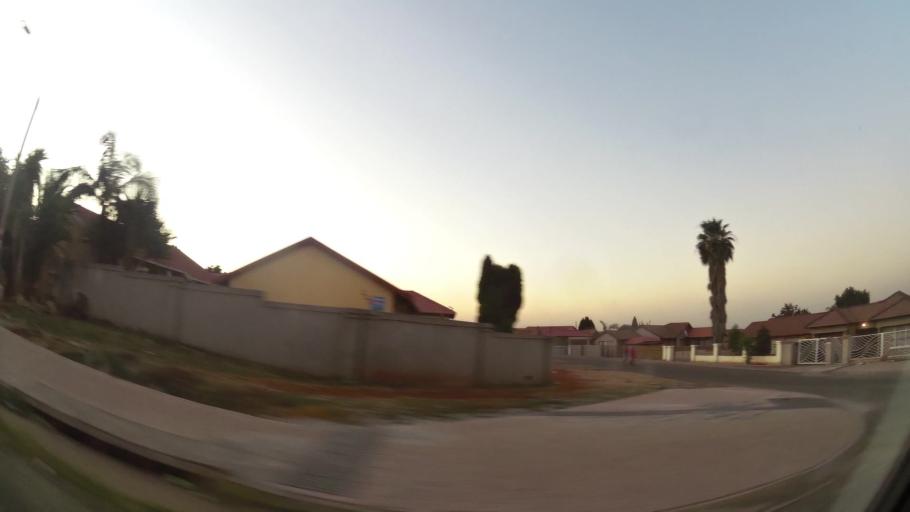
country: ZA
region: North-West
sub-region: Bojanala Platinum District Municipality
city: Rustenburg
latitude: -25.6560
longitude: 27.2095
